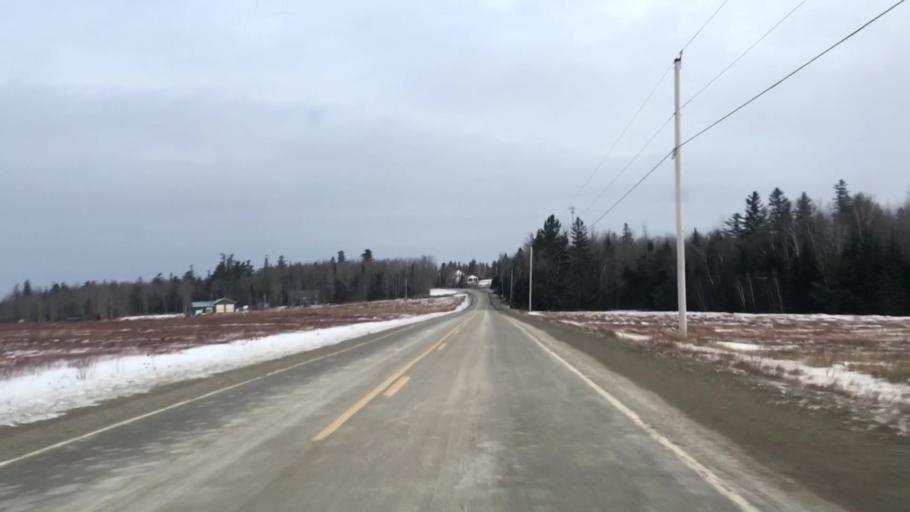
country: US
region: Maine
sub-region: Hancock County
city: Franklin
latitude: 44.7199
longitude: -68.3355
